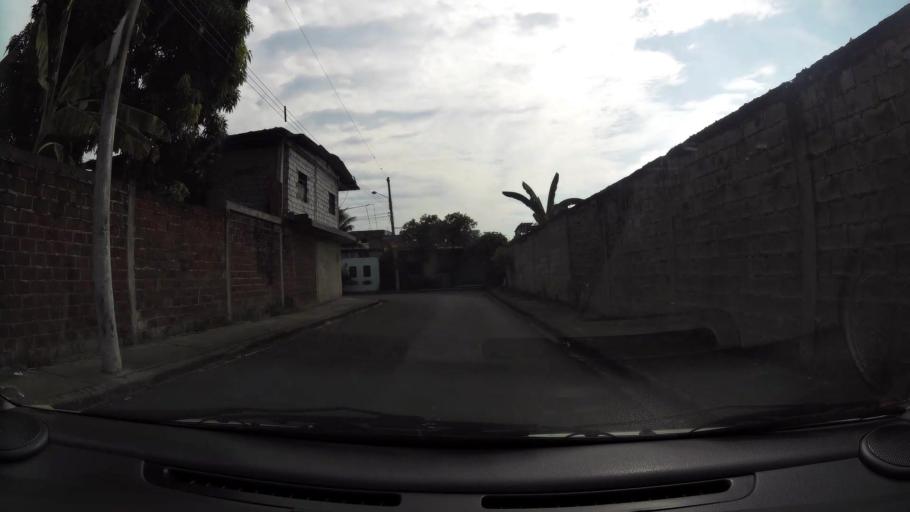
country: EC
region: Guayas
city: Guayaquil
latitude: -2.2598
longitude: -79.9010
